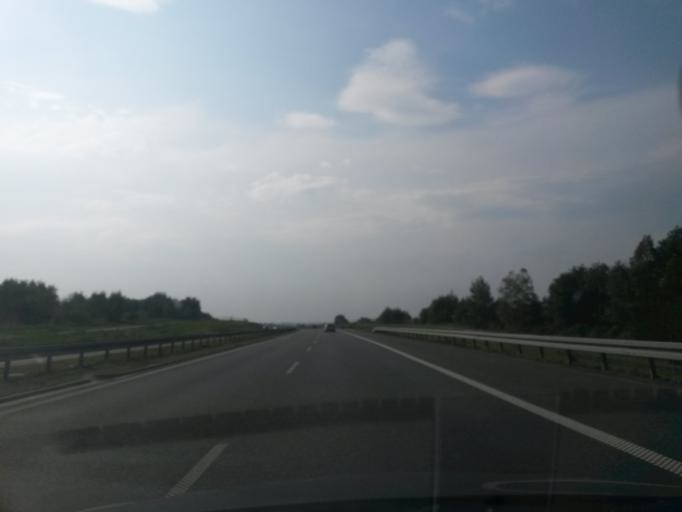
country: PL
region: Lesser Poland Voivodeship
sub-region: Powiat bochenski
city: Borek
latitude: 50.0097
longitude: 20.5166
